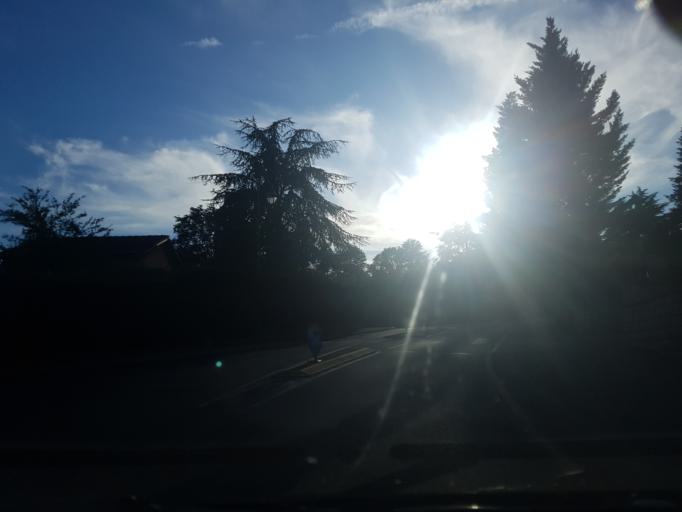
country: FR
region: Rhone-Alpes
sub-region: Departement du Rhone
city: Villefranche-sur-Saone
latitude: 45.9727
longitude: 4.7148
